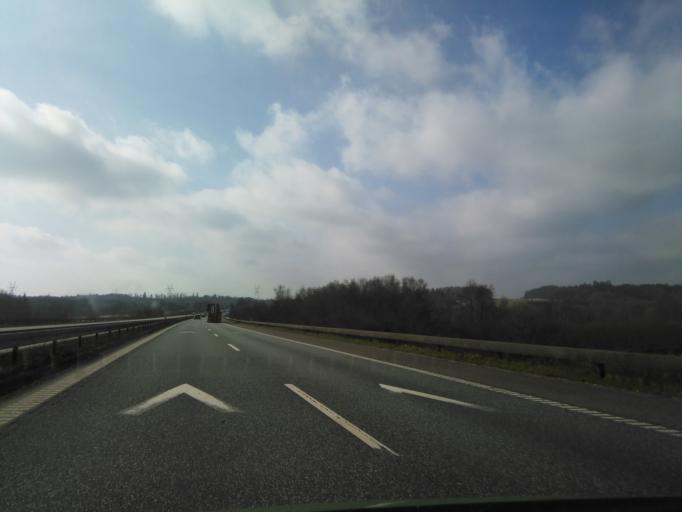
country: DK
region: Central Jutland
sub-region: Horsens Kommune
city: Horsens
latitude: 55.8954
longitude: 9.8082
